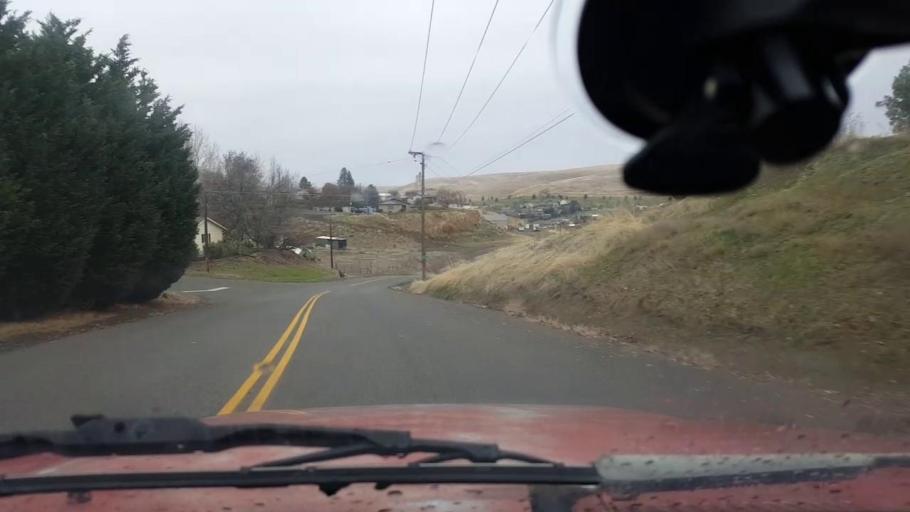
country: US
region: Washington
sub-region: Asotin County
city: Clarkston Heights-Vineland
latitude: 46.3805
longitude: -117.0855
